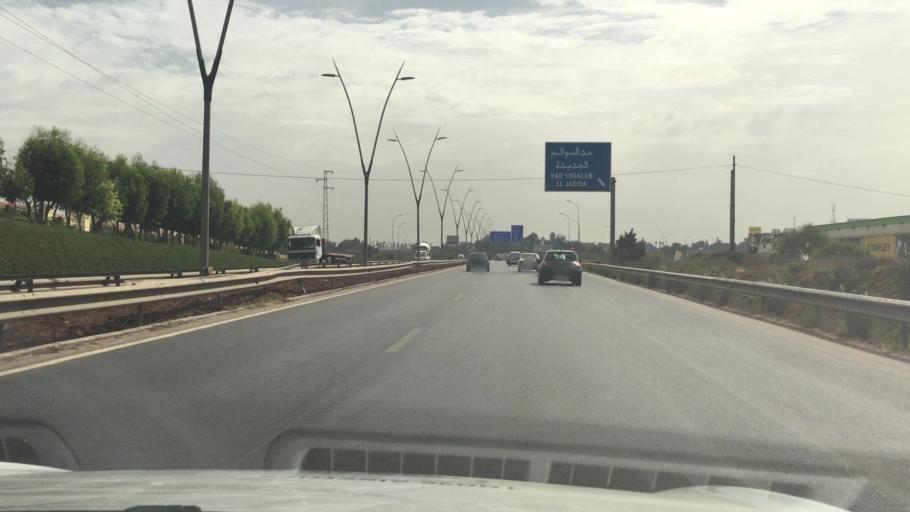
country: MA
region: Grand Casablanca
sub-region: Nouaceur
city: Bouskoura
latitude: 33.5042
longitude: -7.6292
